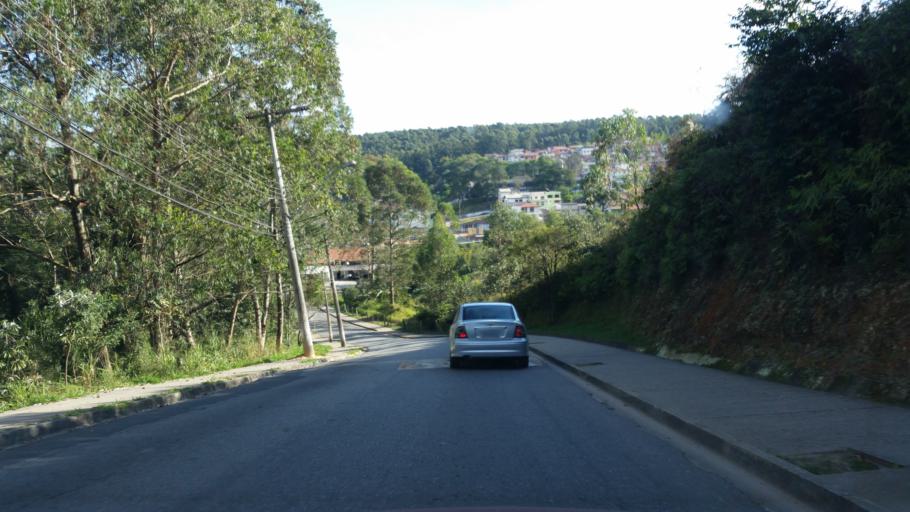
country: BR
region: Sao Paulo
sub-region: Mairinque
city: Mairinque
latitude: -23.5161
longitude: -47.2543
